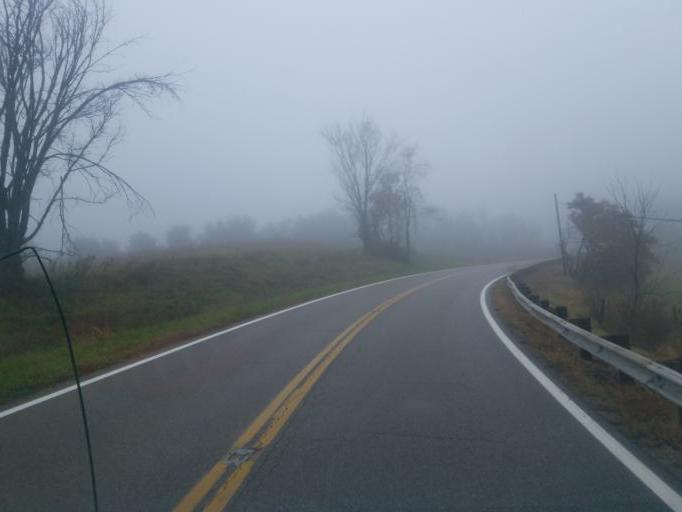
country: US
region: Ohio
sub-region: Morgan County
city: McConnelsville
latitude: 39.5870
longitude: -81.8631
